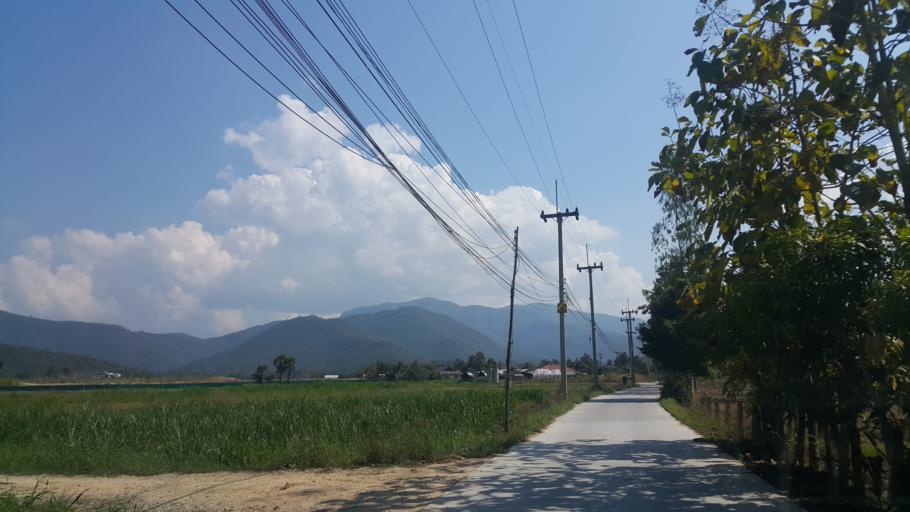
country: TH
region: Lamphun
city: Ban Thi
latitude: 18.6841
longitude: 99.1578
